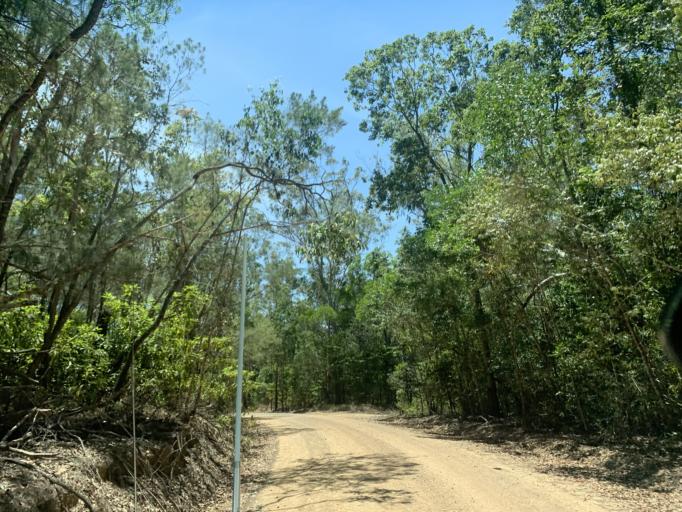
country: AU
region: Queensland
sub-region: Cairns
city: Redlynch
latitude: -16.9241
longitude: 145.6040
